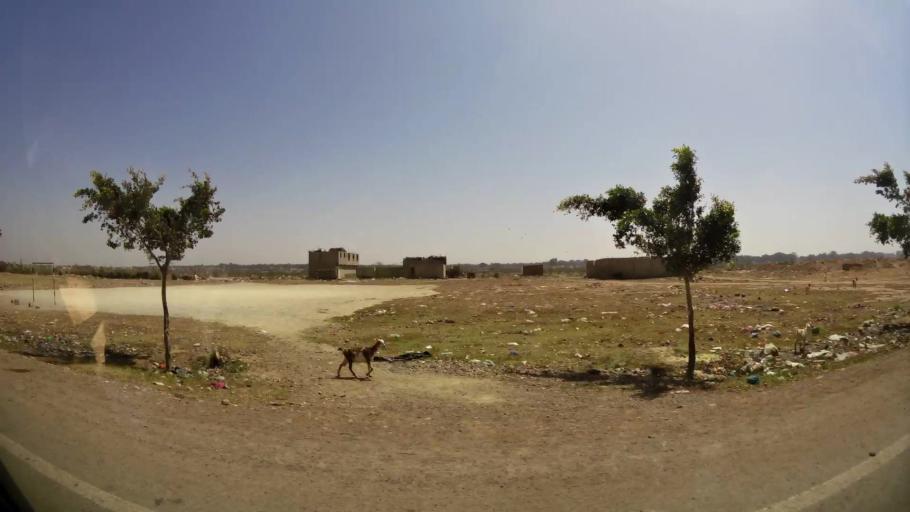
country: MA
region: Souss-Massa-Draa
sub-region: Inezgane-Ait Mellou
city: Inezgane
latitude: 30.3433
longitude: -9.5427
